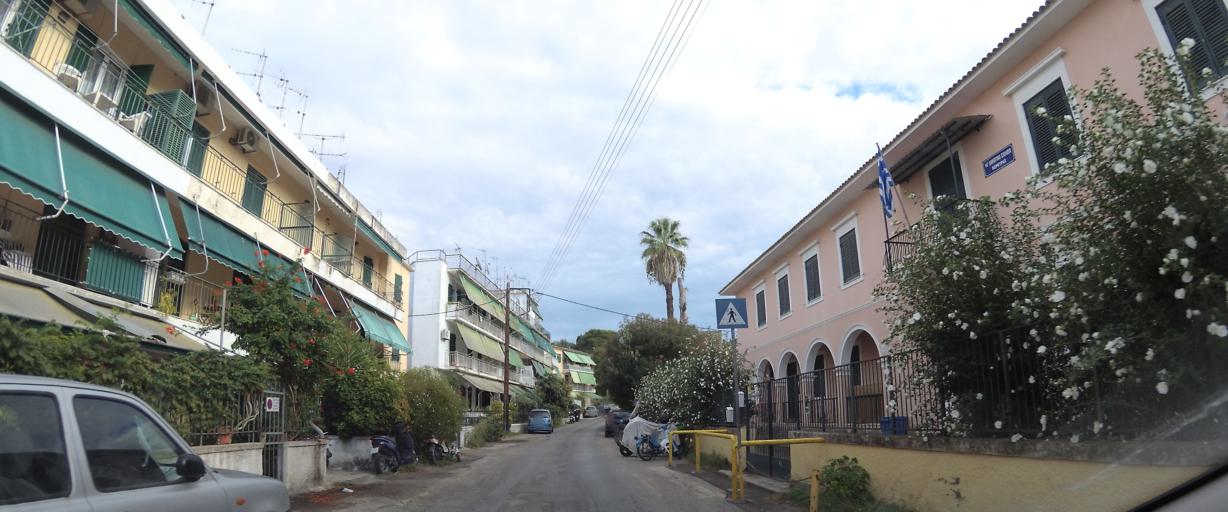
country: GR
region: Ionian Islands
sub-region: Nomos Kerkyras
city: Kerkyra
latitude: 39.6086
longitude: 19.9215
